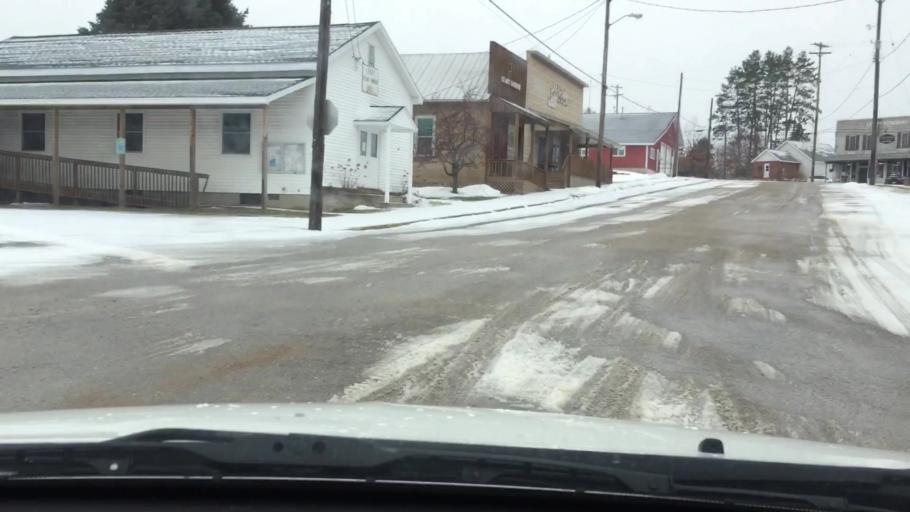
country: US
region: Michigan
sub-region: Osceola County
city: Reed City
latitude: 44.0383
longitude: -85.4516
